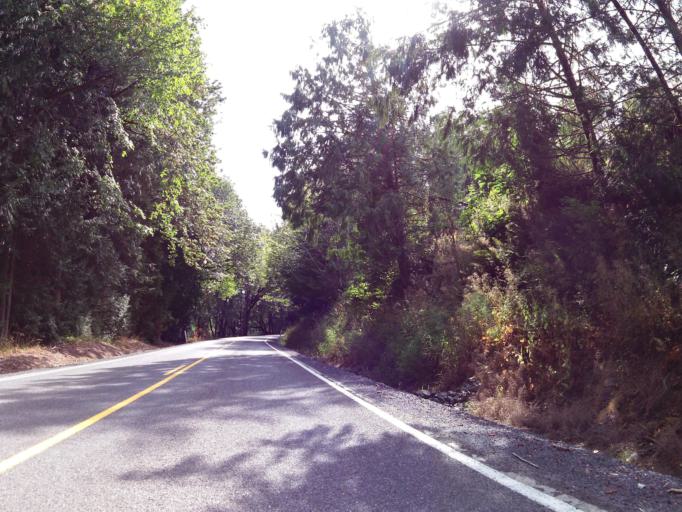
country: US
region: Washington
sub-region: Lewis County
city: Napavine
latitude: 46.5578
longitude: -122.9596
